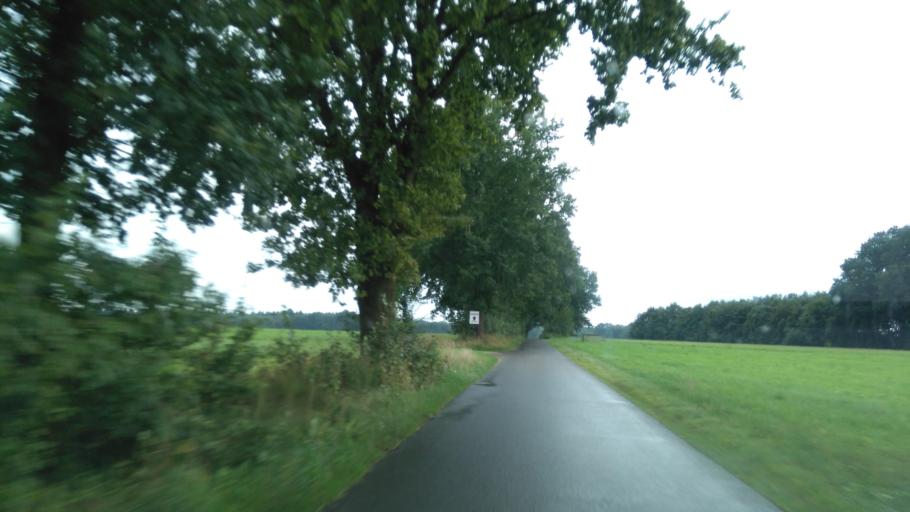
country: DE
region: Lower Saxony
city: Walsrode
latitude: 52.8914
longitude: 9.6057
